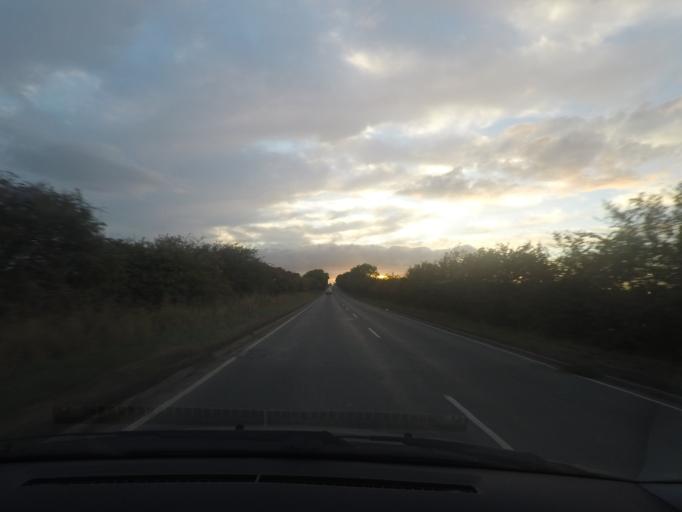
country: GB
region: England
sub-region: North Lincolnshire
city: Barnetby le Wold
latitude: 53.5824
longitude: -0.3963
